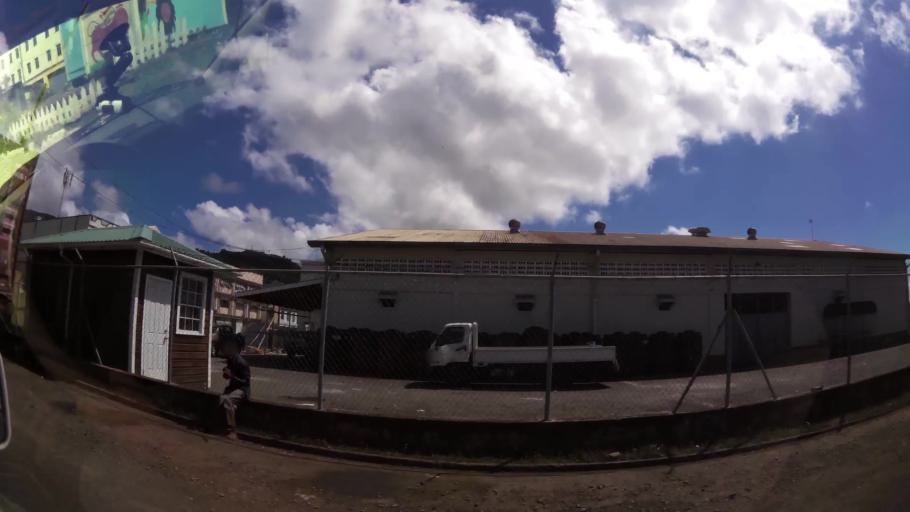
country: VC
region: Saint George
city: Kingstown Park
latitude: 13.1562
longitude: -61.2300
